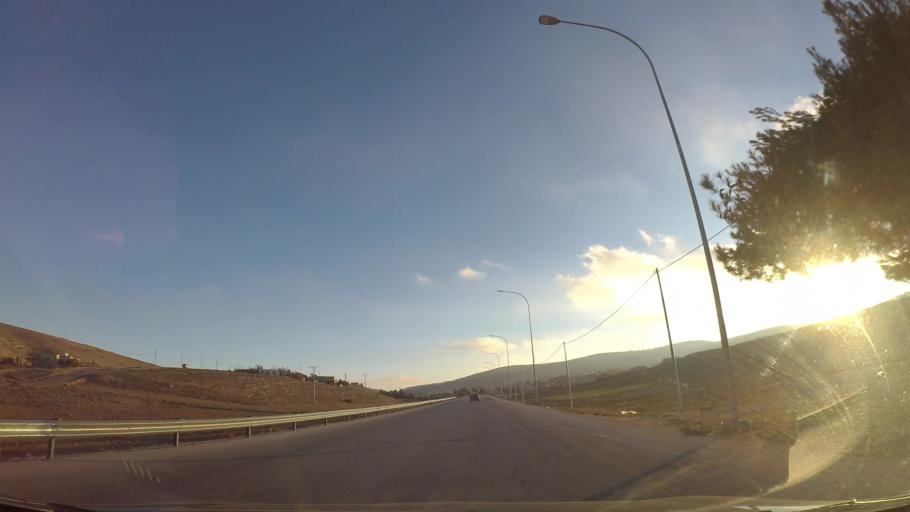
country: JO
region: Ma'an
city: Petra
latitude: 30.4437
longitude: 35.5215
